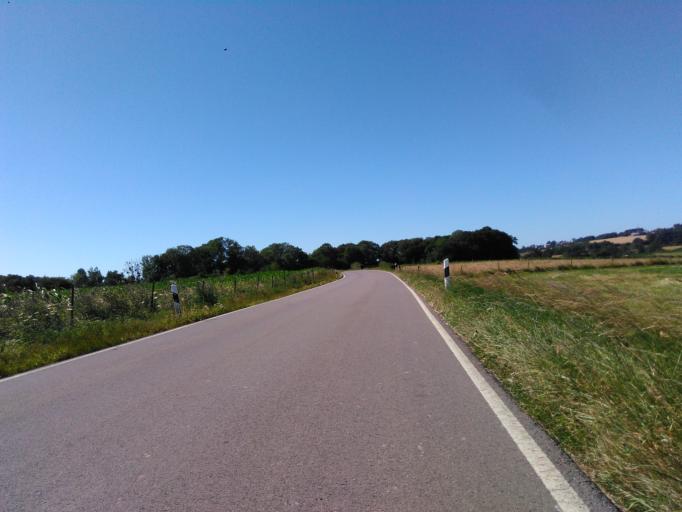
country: LU
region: Luxembourg
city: Schouweiler
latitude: 49.5668
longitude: 5.9724
